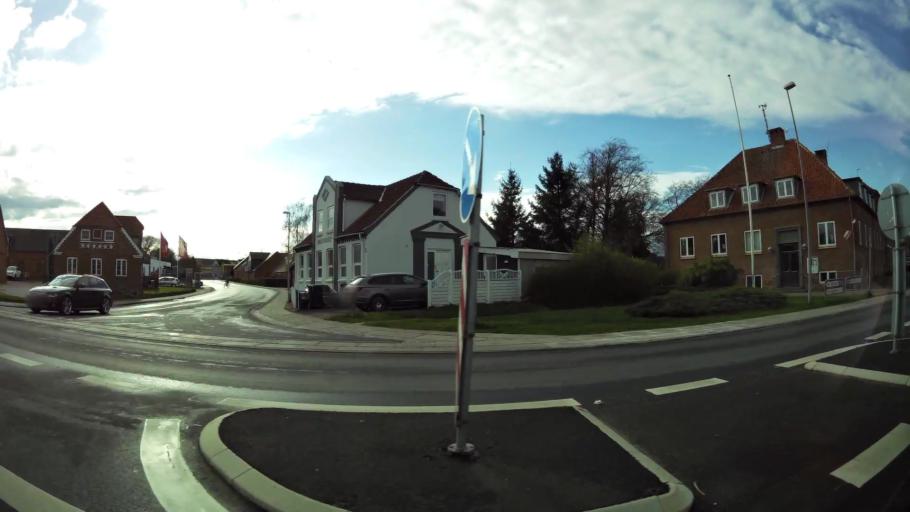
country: DK
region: Central Jutland
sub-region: Syddjurs Kommune
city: Hornslet
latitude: 56.3149
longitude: 10.3210
